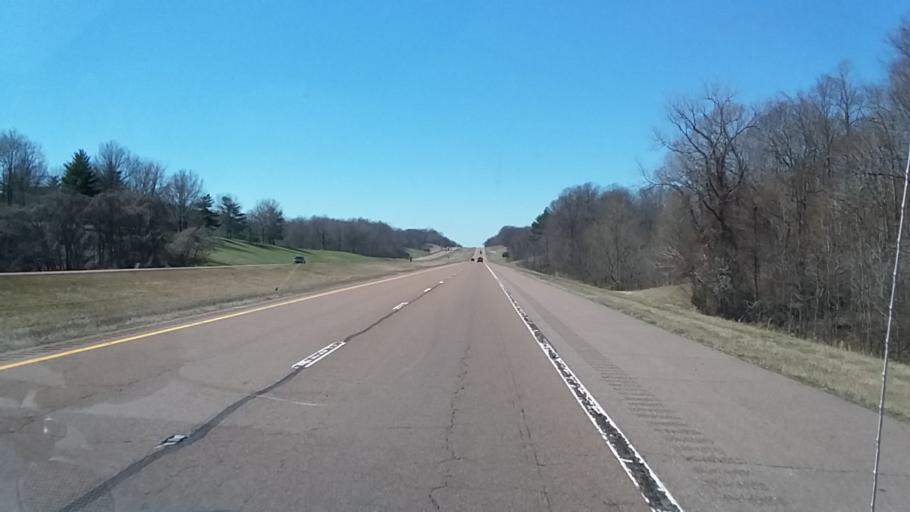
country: US
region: Tennessee
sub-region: Dyer County
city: Dyersburg
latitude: 36.0723
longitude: -89.4674
